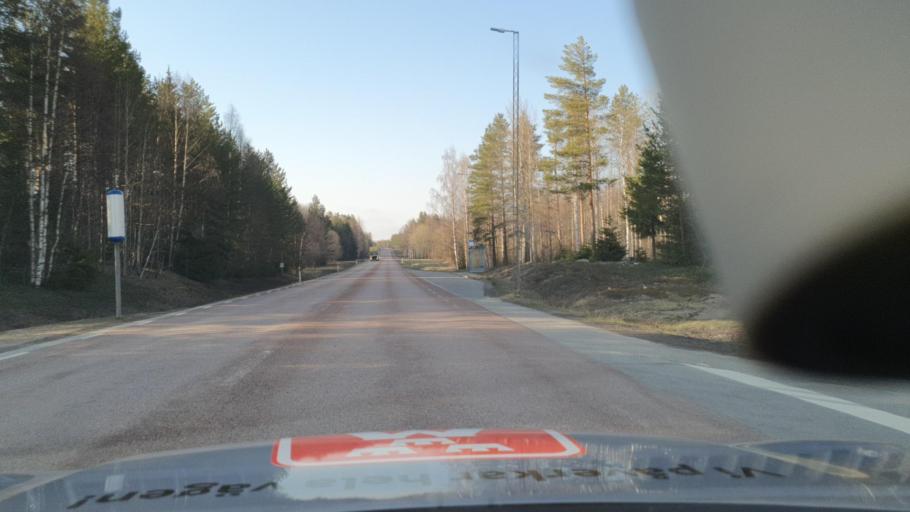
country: SE
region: Vaesterbotten
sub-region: Skelleftea Kommun
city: Burea
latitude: 64.6192
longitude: 21.1785
